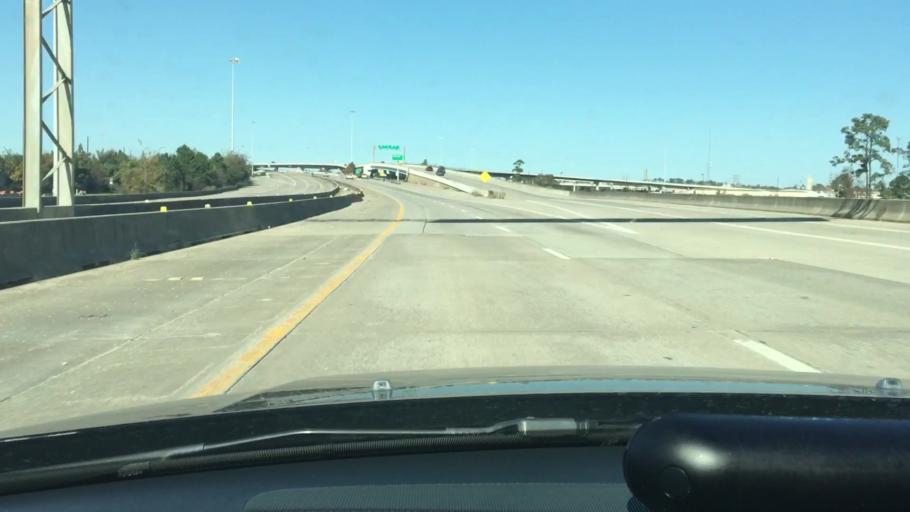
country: US
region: Texas
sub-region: Harris County
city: Cloverleaf
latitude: 29.7648
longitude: -95.1480
